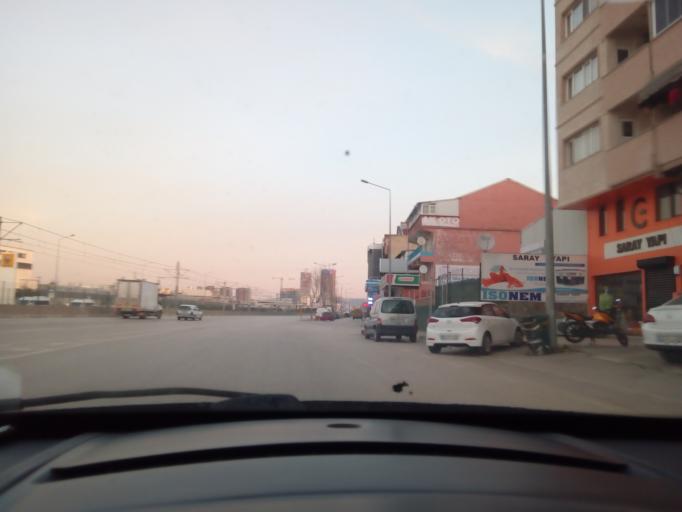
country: TR
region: Bursa
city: Niluefer
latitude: 40.2540
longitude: 28.9543
